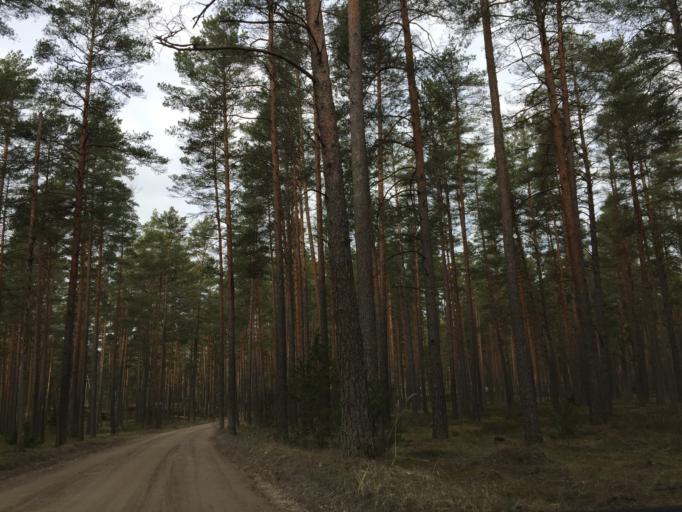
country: LV
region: Garkalne
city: Garkalne
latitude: 57.0677
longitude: 24.4676
